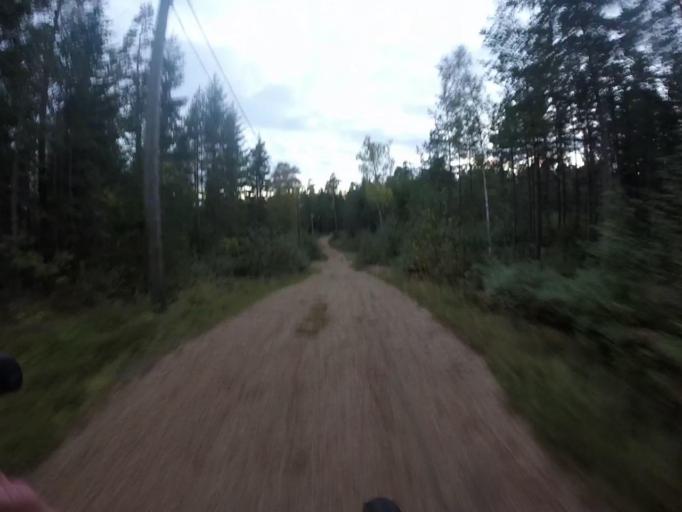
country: SE
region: Vaestra Goetaland
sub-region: Trollhattan
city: Trollhattan
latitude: 58.2922
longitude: 12.2627
